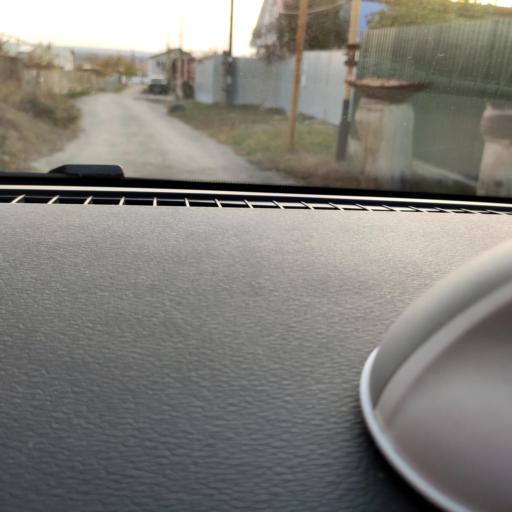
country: RU
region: Samara
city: Samara
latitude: 53.1727
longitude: 50.1687
